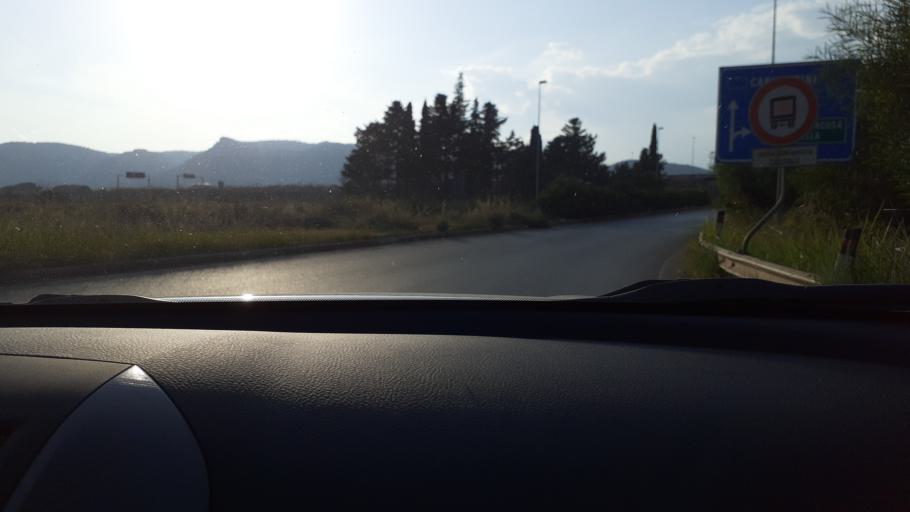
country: IT
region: Sicily
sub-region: Provincia di Siracusa
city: Cassibile
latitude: 36.9718
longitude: 15.1916
